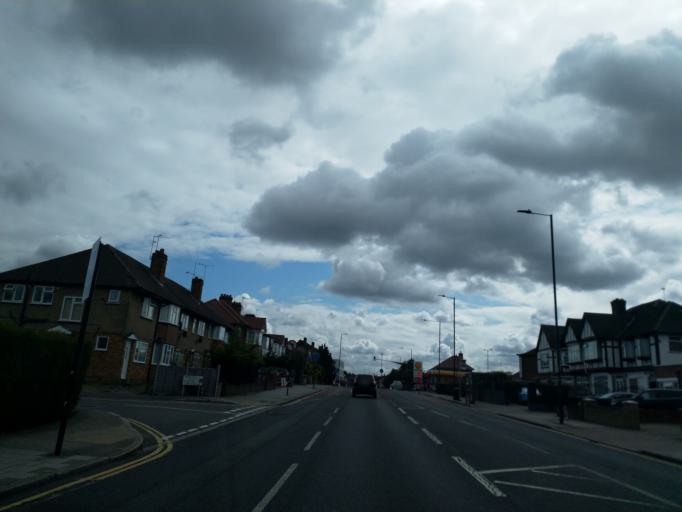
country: GB
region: England
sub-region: Greater London
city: Edgware
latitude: 51.5856
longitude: -0.2865
